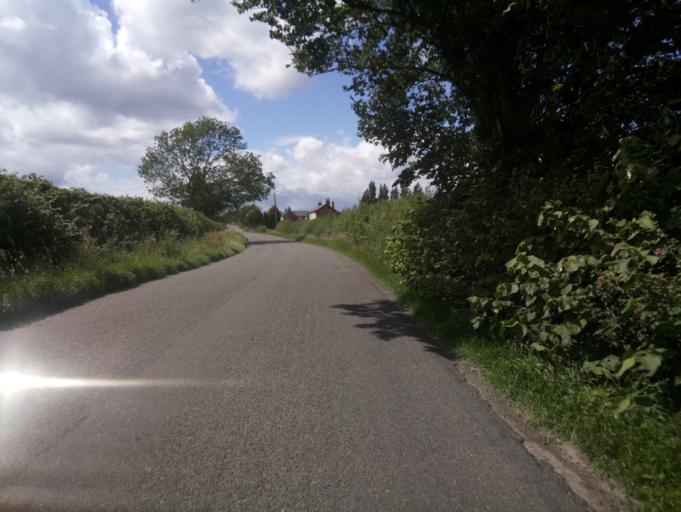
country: GB
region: England
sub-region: Nottinghamshire
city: Arnold
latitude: 53.0075
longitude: -1.0874
